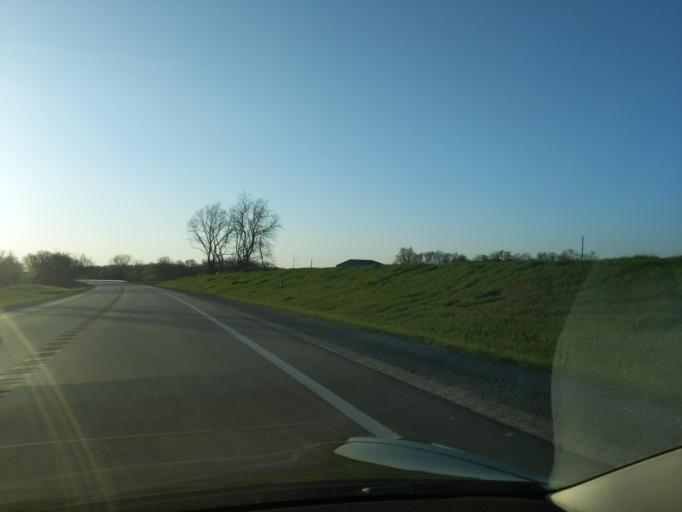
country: US
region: Michigan
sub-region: Washtenaw County
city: Chelsea
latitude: 42.3877
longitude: -84.0894
